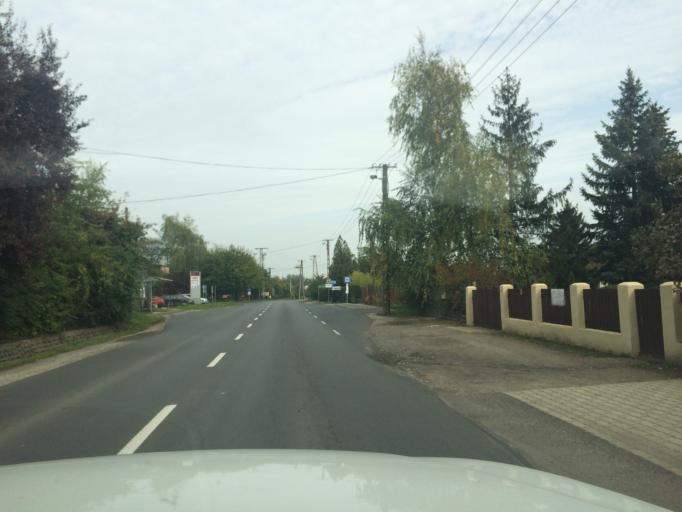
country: HU
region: Szabolcs-Szatmar-Bereg
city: Kotaj
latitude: 48.0077
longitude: 21.7373
